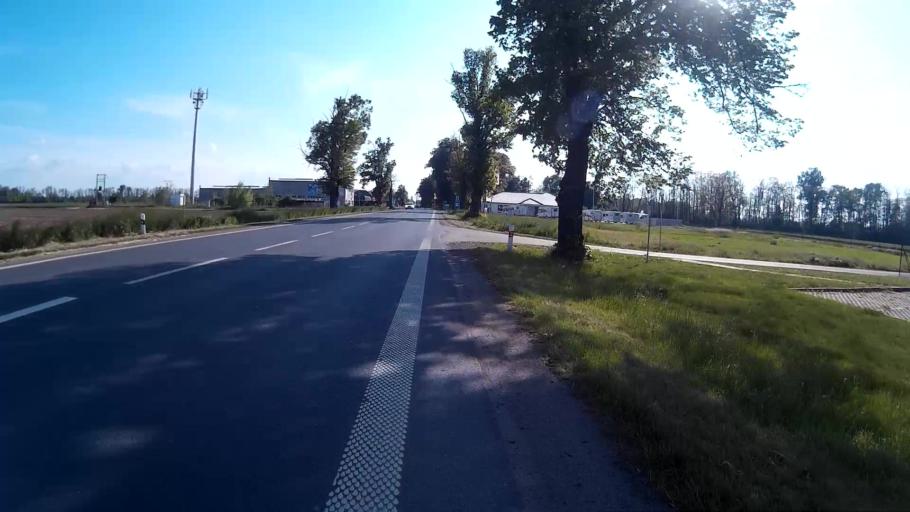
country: CZ
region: South Moravian
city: Pohorelice
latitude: 48.9895
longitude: 16.5385
